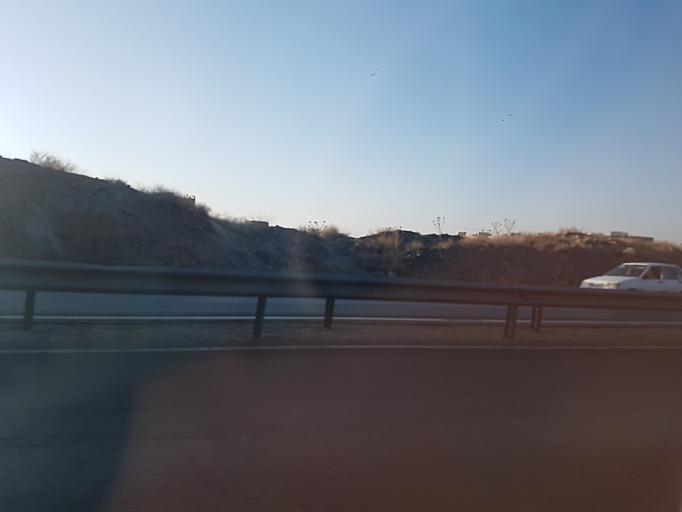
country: IR
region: Markazi
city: Arak
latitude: 34.0686
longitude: 49.7082
